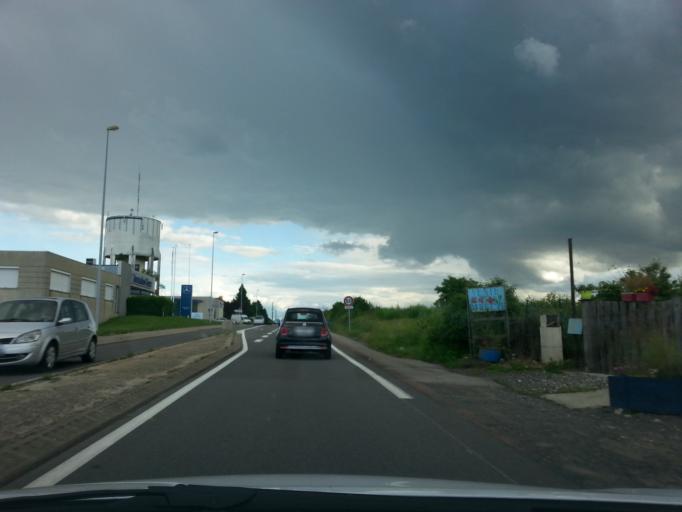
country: FR
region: Rhone-Alpes
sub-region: Departement du Rhone
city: Rillieux-la-Pape
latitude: 45.8273
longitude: 4.9060
